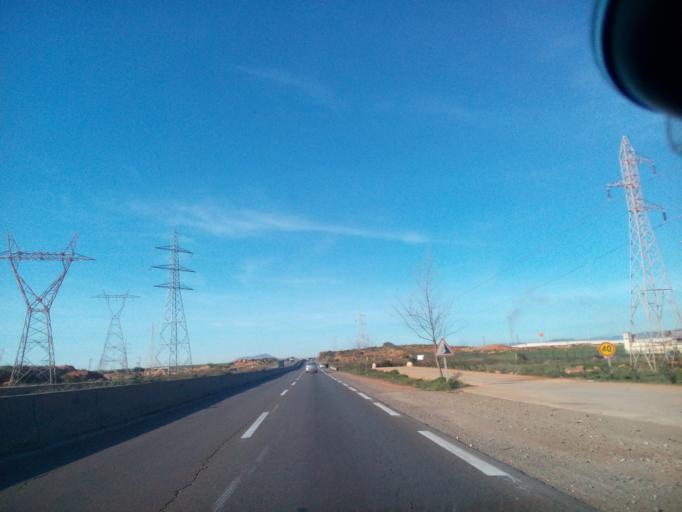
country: DZ
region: Oran
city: Ain el Bya
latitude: 35.8011
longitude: -0.3121
